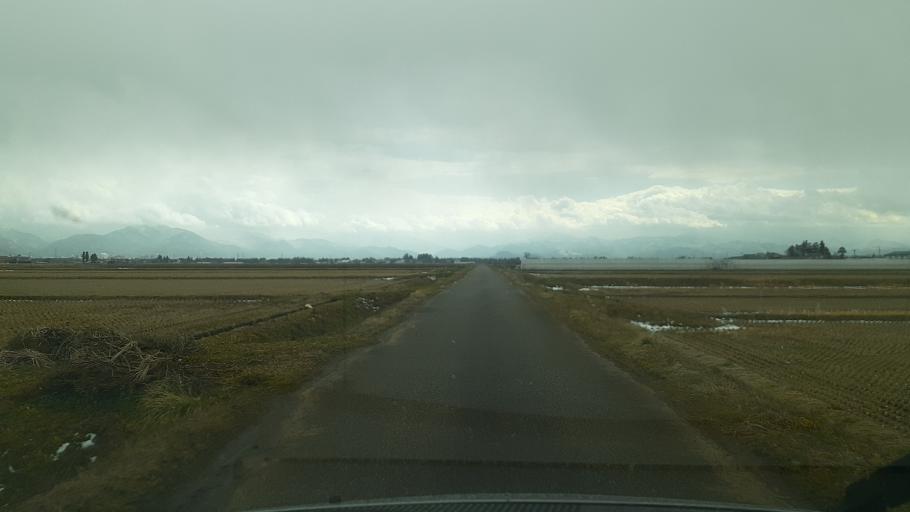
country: JP
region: Fukushima
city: Kitakata
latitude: 37.5492
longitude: 139.9000
